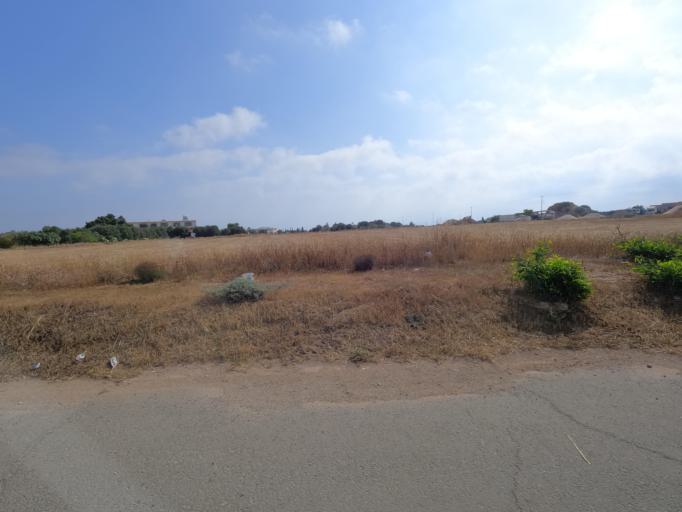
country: CY
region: Ammochostos
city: Paralimni
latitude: 35.0268
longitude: 34.0082
